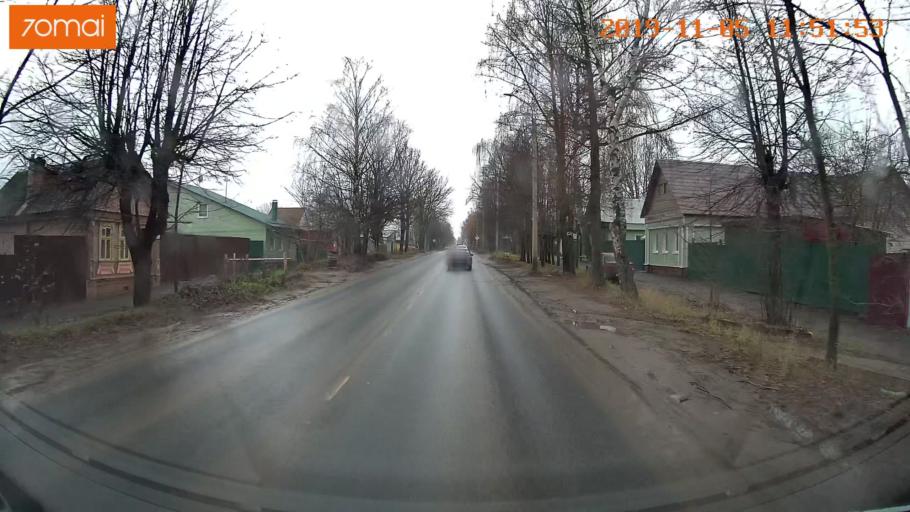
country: RU
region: Ivanovo
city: Bogorodskoye
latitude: 57.0032
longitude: 41.0288
